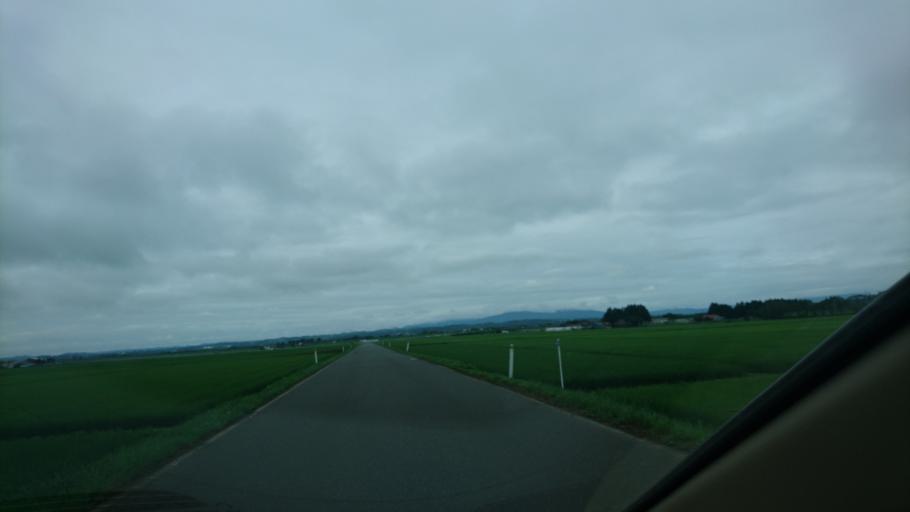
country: JP
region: Iwate
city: Mizusawa
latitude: 39.0646
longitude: 141.1778
